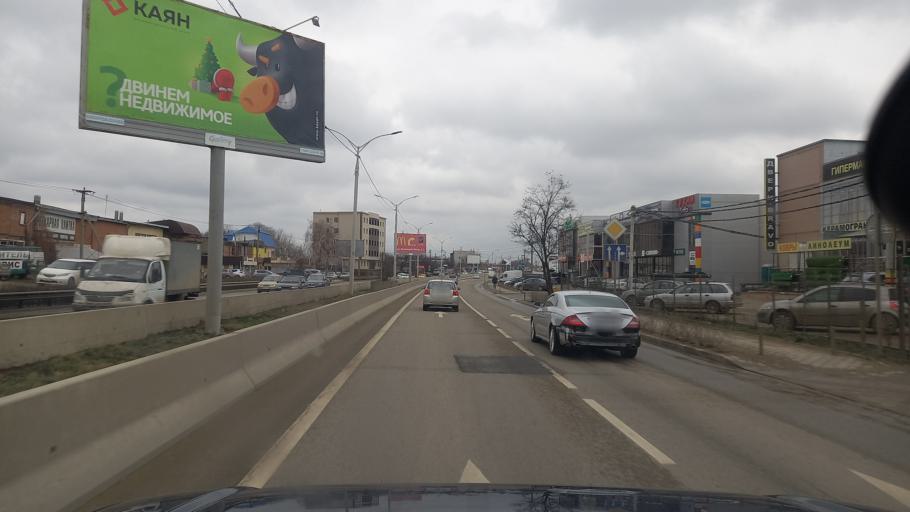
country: RU
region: Krasnodarskiy
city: Pashkovskiy
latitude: 45.0437
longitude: 39.1189
